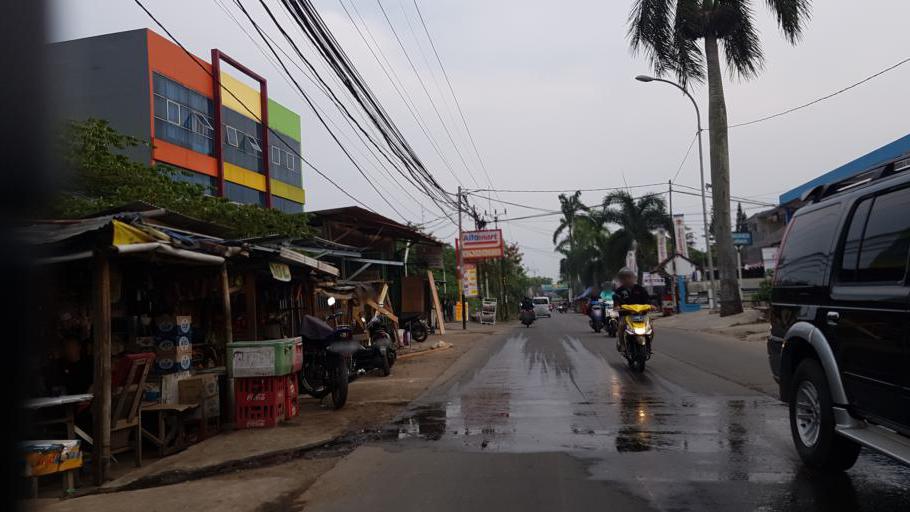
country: ID
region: West Java
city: Sawangan
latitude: -6.3919
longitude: 106.7948
